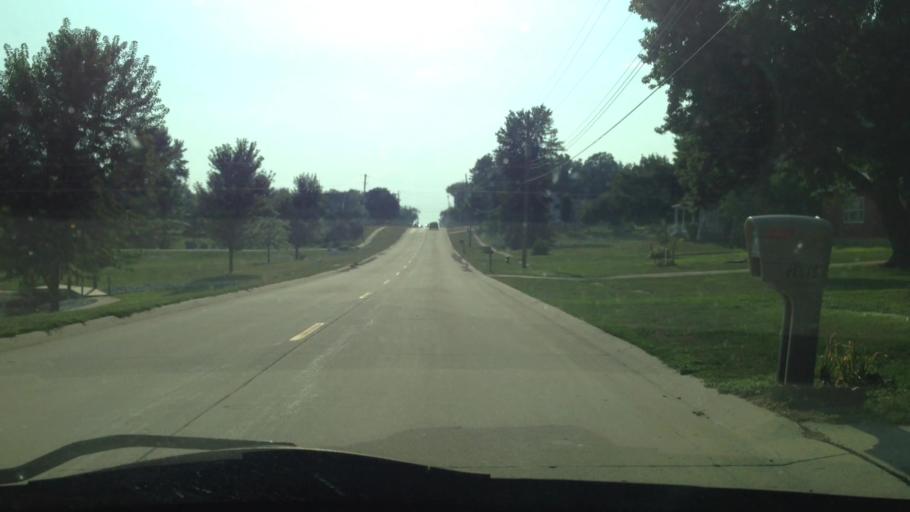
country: US
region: Iowa
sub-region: Henry County
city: Winfield
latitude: 41.2140
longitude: -91.5327
